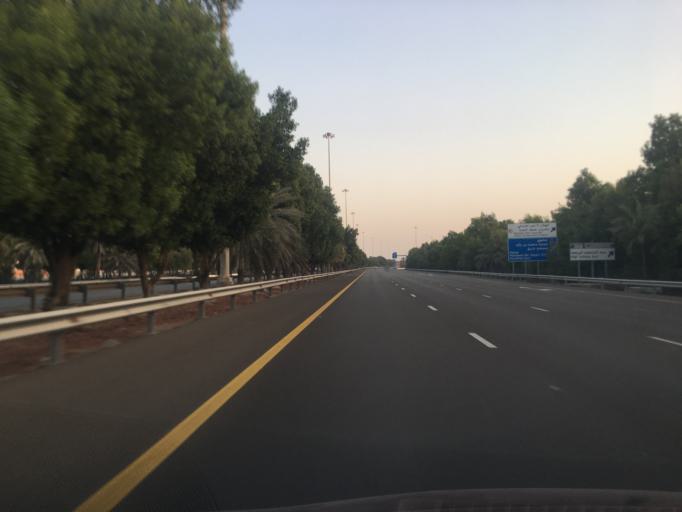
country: AE
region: Abu Dhabi
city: Abu Dhabi
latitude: 24.3448
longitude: 54.5738
